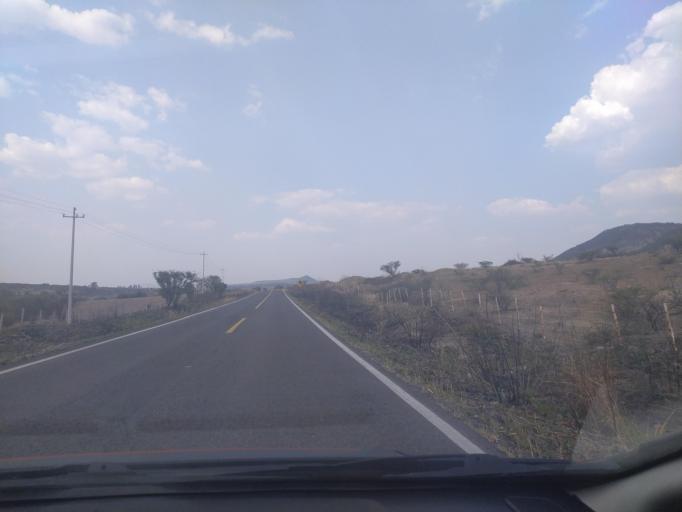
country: MX
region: Guanajuato
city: Ciudad Manuel Doblado
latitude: 20.6333
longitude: -101.9766
